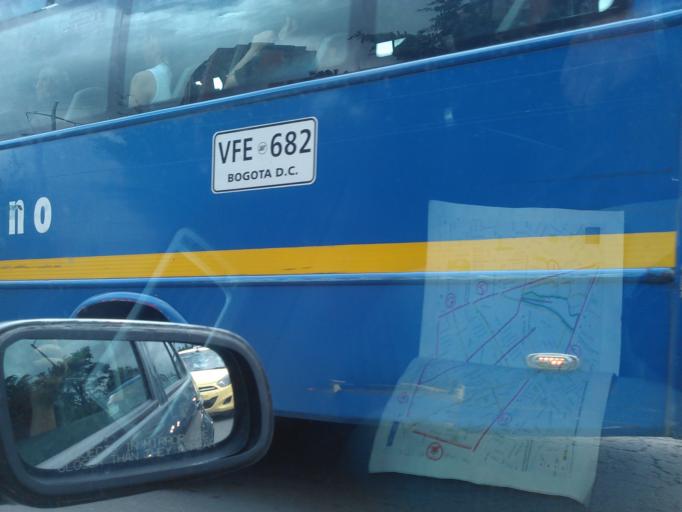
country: CO
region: Bogota D.C.
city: Bogota
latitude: 4.6226
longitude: -74.1247
